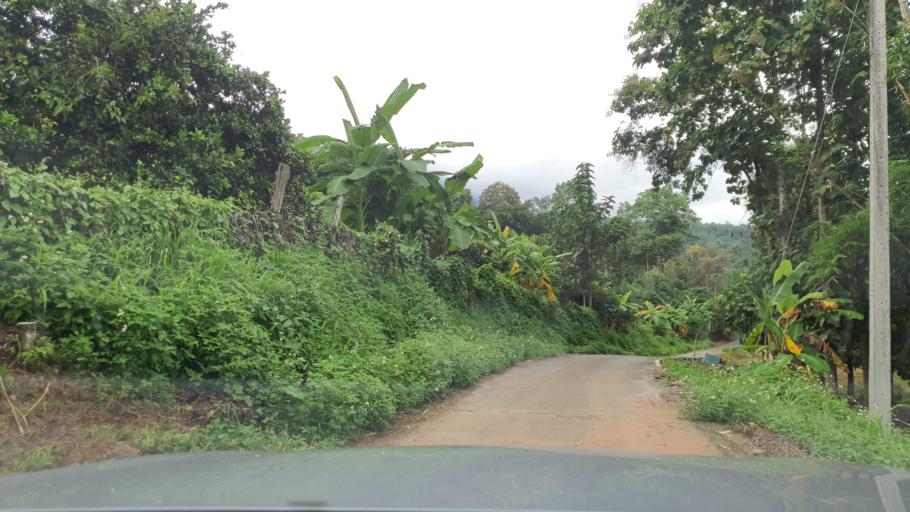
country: TH
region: Chiang Mai
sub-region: Amphoe Chiang Dao
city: Chiang Dao
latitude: 19.3336
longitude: 98.9280
